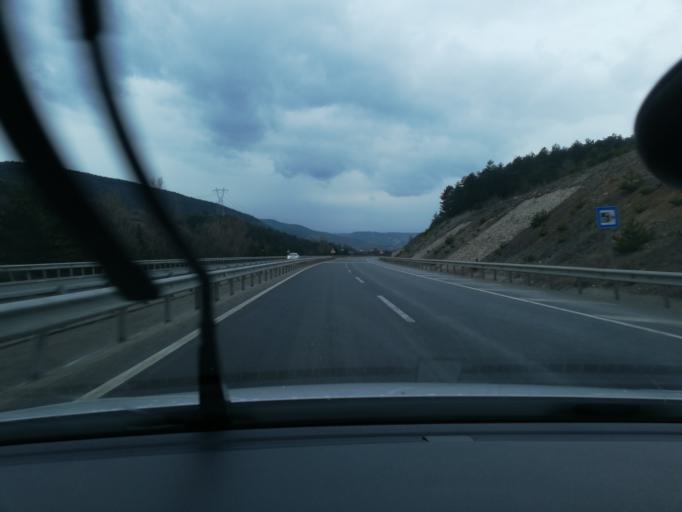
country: TR
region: Bolu
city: Yenicaga
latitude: 40.7498
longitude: 31.8964
